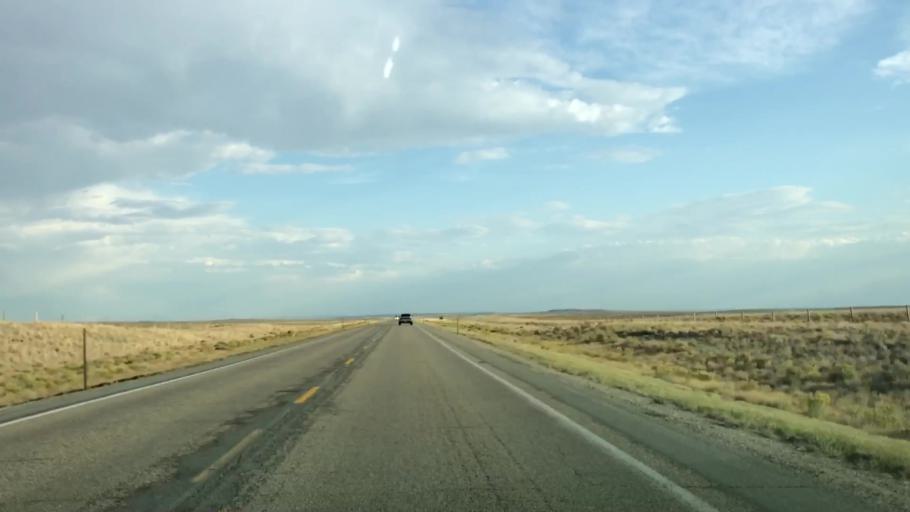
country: US
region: Wyoming
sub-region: Sublette County
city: Pinedale
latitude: 42.4055
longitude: -109.5493
